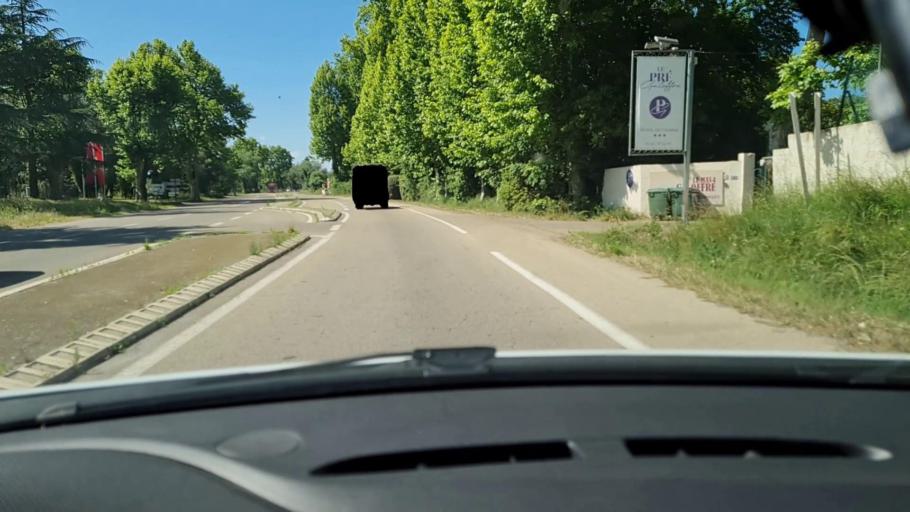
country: FR
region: Languedoc-Roussillon
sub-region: Departement du Gard
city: Caissargues
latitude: 43.7877
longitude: 4.3527
